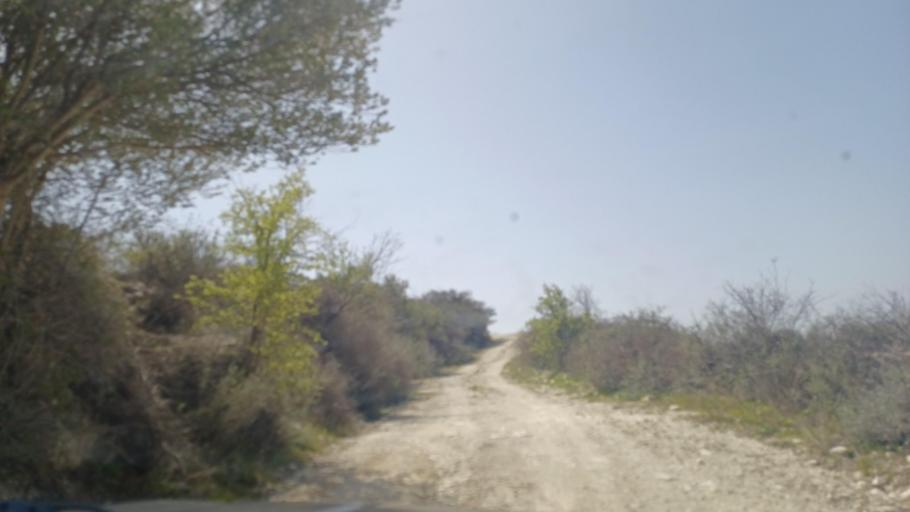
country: CY
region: Limassol
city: Pachna
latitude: 34.8596
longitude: 32.7353
